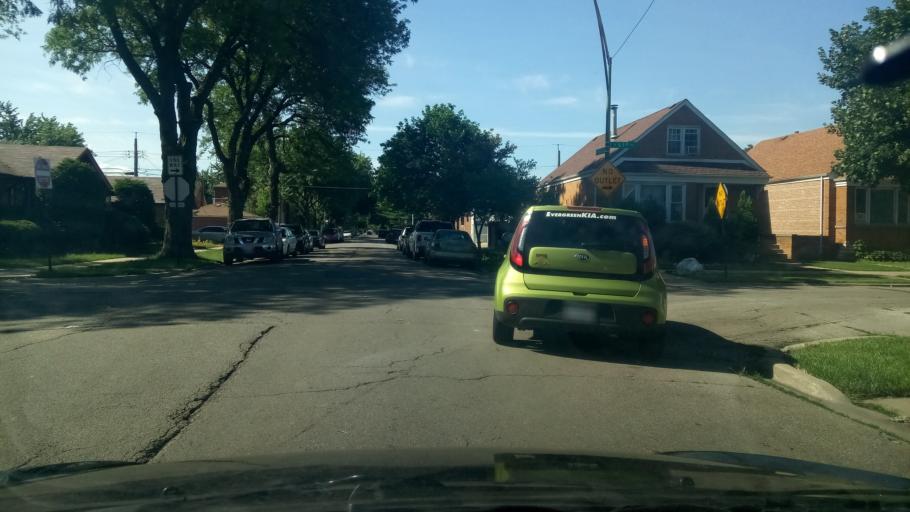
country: US
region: Illinois
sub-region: Cook County
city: Hometown
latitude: 41.7780
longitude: -87.7203
